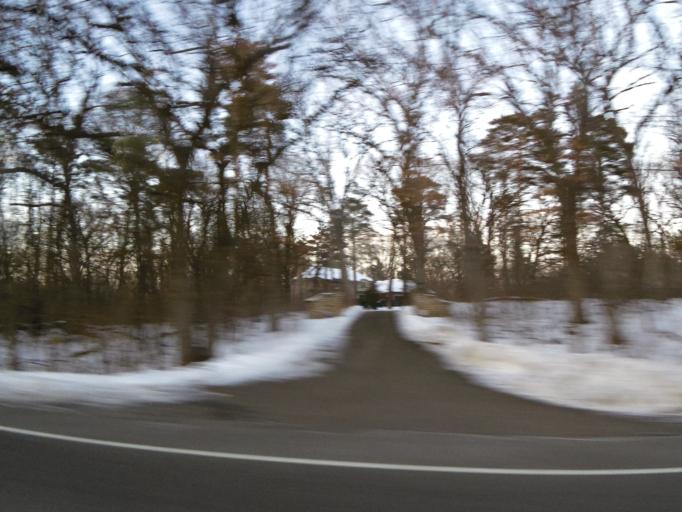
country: US
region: Minnesota
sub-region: Washington County
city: Dellwood
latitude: 45.0900
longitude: -92.9583
